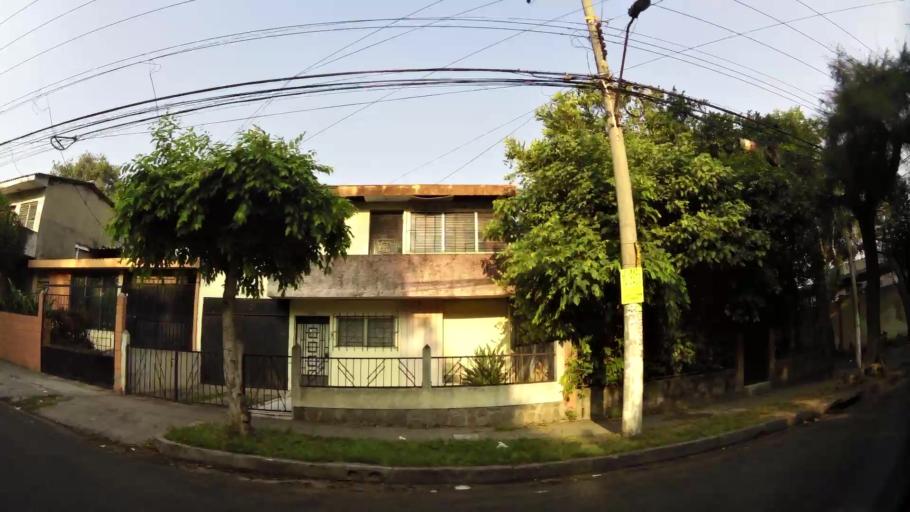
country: SV
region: San Salvador
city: San Salvador
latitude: 13.6795
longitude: -89.1992
